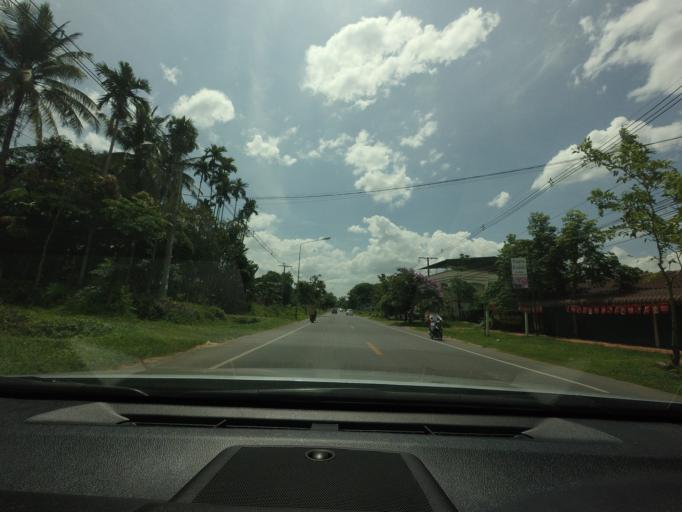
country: TH
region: Yala
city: Krong Pi Nang
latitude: 6.4630
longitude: 101.3294
